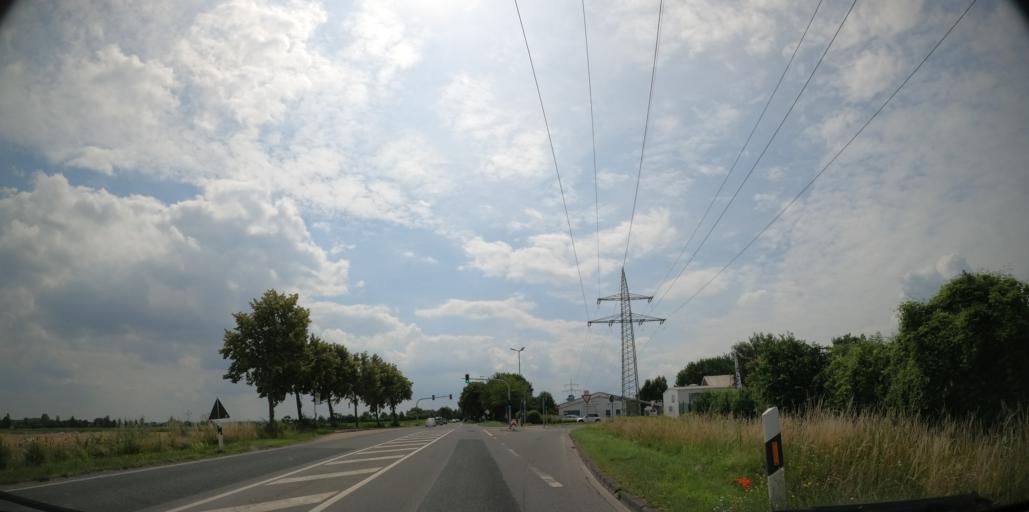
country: DE
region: North Rhine-Westphalia
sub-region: Regierungsbezirk Arnsberg
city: Lippstadt
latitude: 51.6549
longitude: 8.3675
